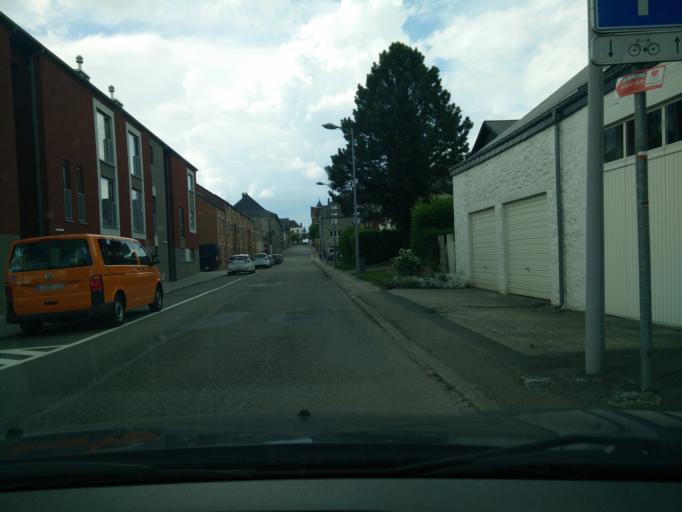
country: BE
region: Wallonia
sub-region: Province de Namur
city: Philippeville
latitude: 50.1940
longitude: 4.5453
